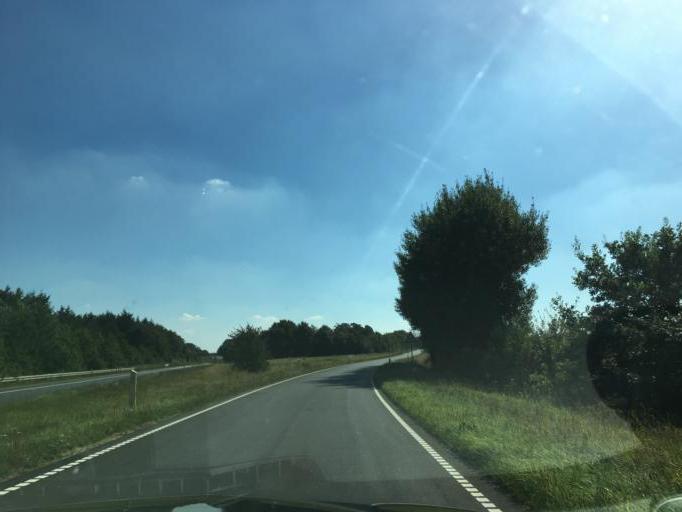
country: DK
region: South Denmark
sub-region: Kolding Kommune
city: Lunderskov
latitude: 55.4963
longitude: 9.2938
